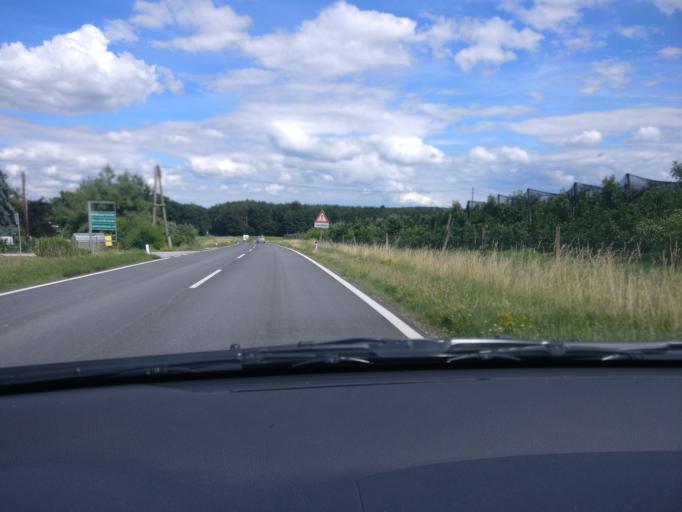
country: AT
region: Styria
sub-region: Politischer Bezirk Hartberg-Fuerstenfeld
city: Dienersdorf
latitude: 47.2132
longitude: 15.8639
